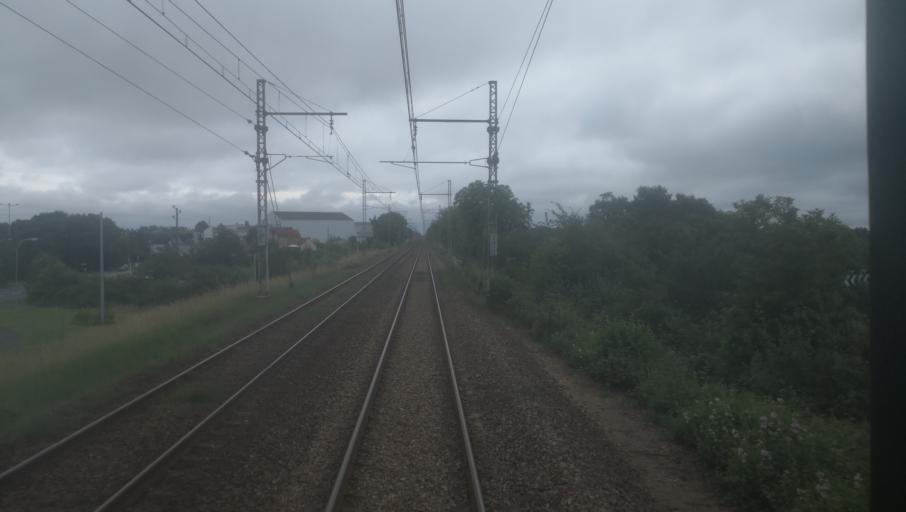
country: FR
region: Centre
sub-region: Departement de l'Indre
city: Saint-Maur
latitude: 46.7951
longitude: 1.6641
